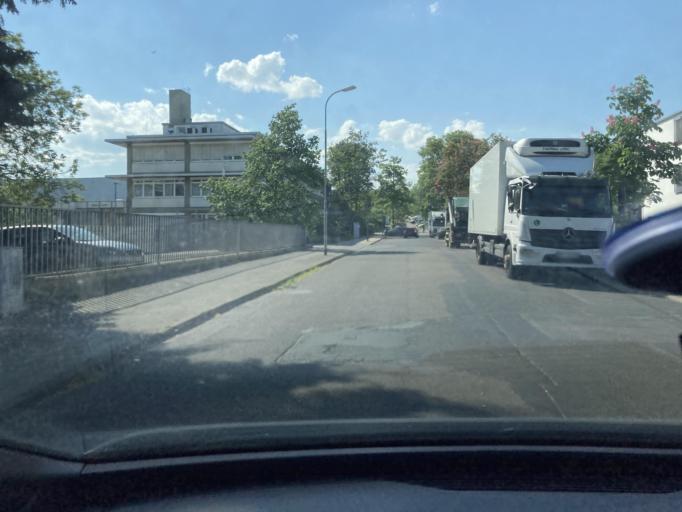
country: DE
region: Hesse
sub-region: Regierungsbezirk Darmstadt
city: Offenbach
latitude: 50.0876
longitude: 8.7467
